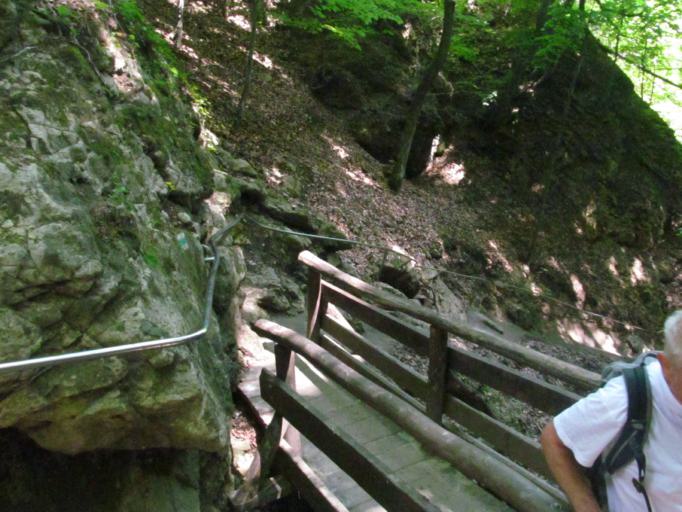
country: HU
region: Pest
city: Pilisszentkereszt
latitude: 47.7371
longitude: 18.8919
